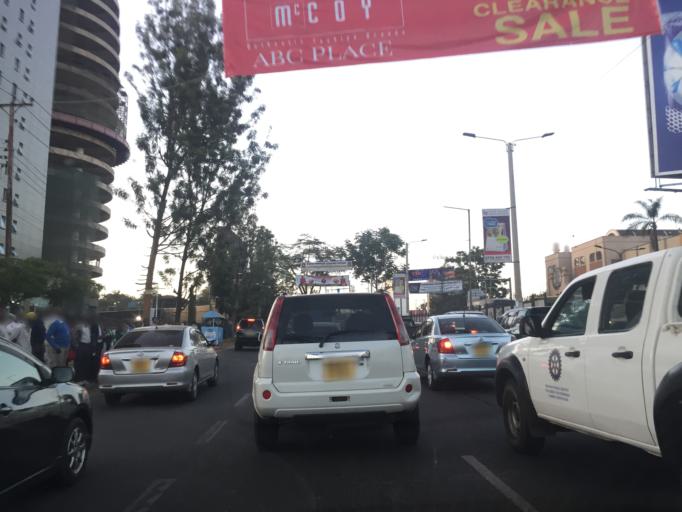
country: KE
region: Nairobi Area
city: Nairobi
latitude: -1.2657
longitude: 36.8027
